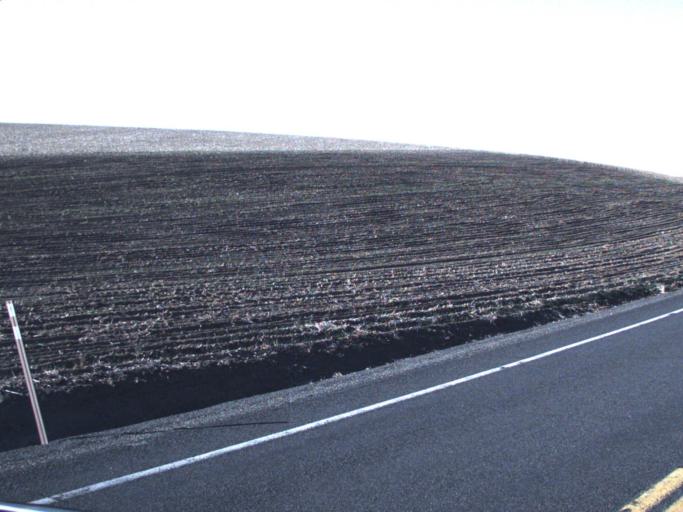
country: US
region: Washington
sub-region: Adams County
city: Ritzville
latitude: 47.0022
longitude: -118.3454
